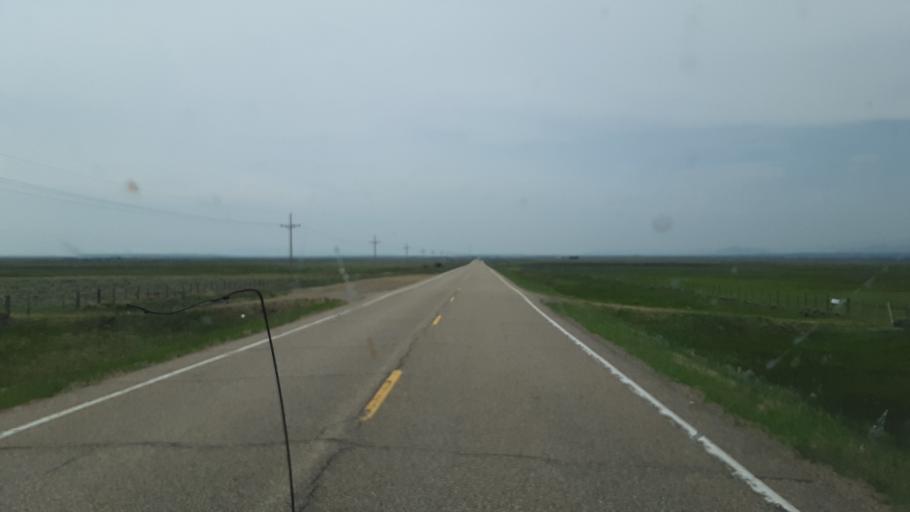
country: US
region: Colorado
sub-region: Jackson County
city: Walden
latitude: 40.8979
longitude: -106.2972
